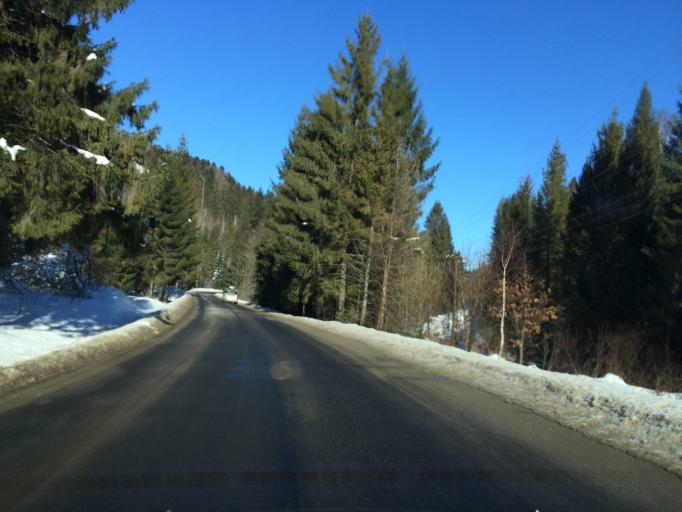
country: PL
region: Subcarpathian Voivodeship
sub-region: Powiat leski
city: Cisna
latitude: 49.2118
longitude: 22.3633
